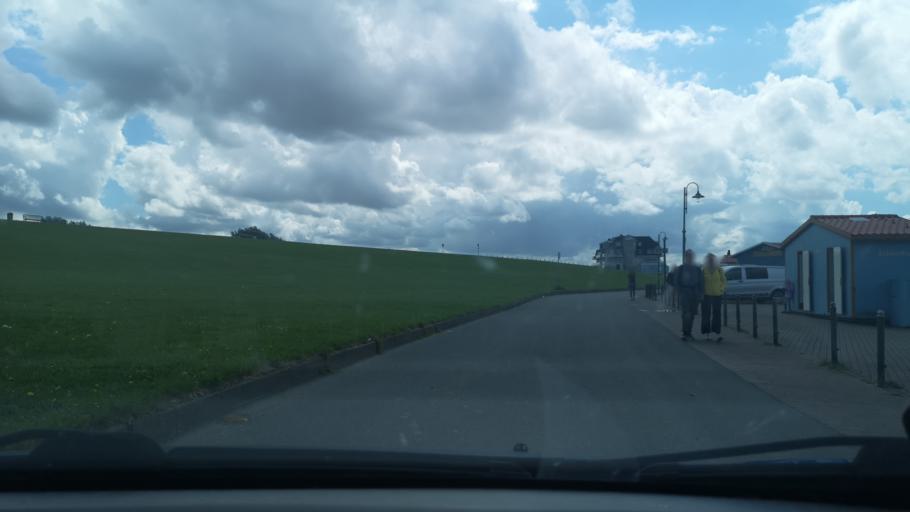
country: DE
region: Lower Saxony
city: Wremen
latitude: 53.6485
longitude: 8.4950
